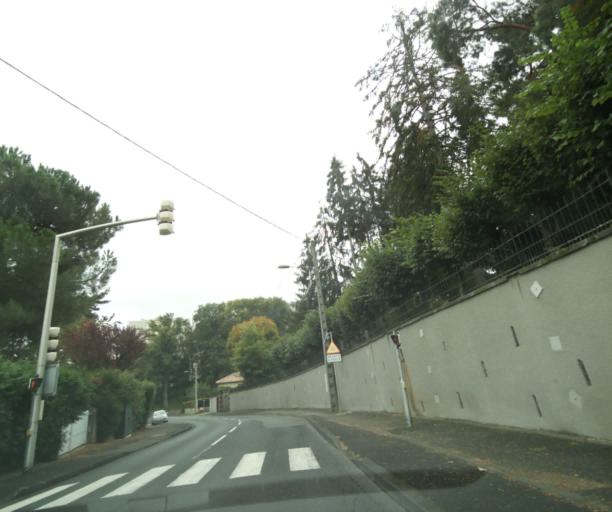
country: FR
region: Auvergne
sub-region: Departement du Puy-de-Dome
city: Durtol
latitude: 45.7903
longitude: 3.0537
